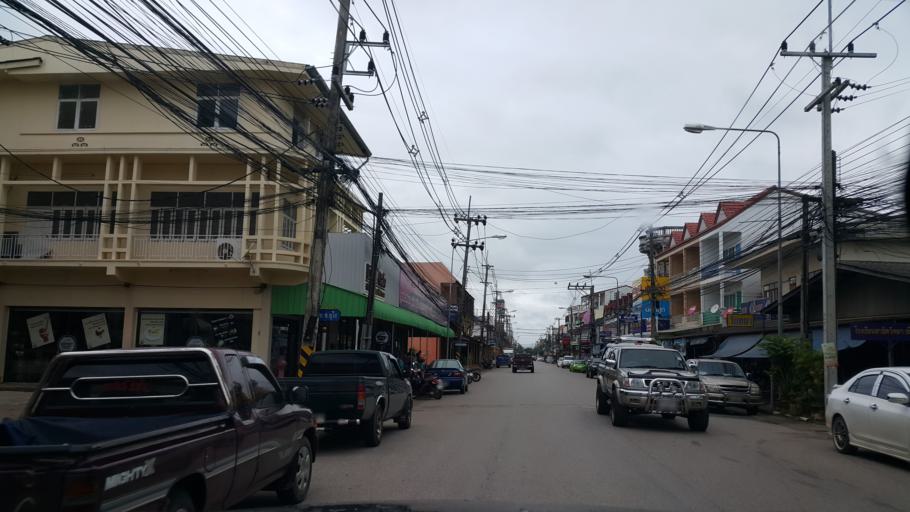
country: TH
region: Phayao
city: Chiang Kham
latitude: 19.5264
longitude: 100.3026
